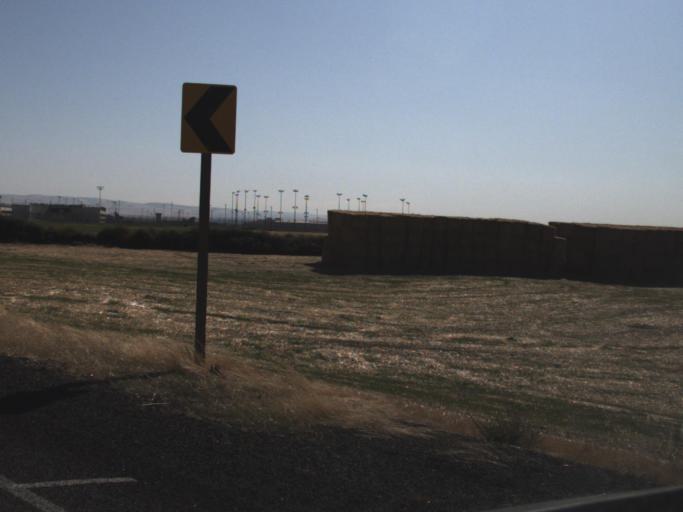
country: US
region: Washington
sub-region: Walla Walla County
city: Walla Walla
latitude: 46.0863
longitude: -118.3670
